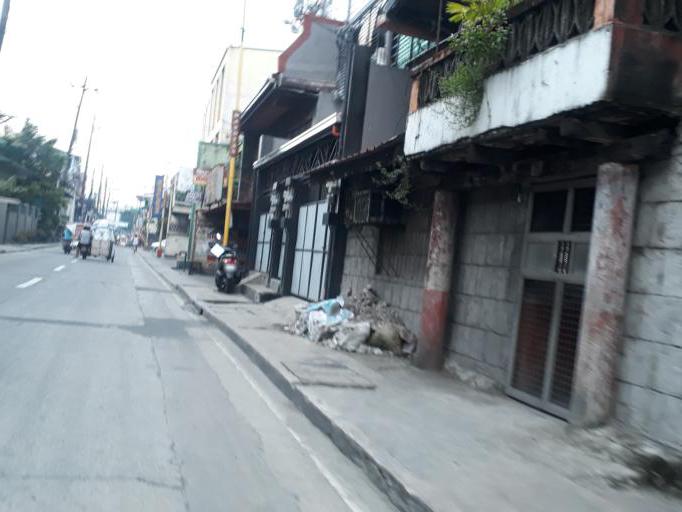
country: PH
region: Metro Manila
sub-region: Caloocan City
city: Niugan
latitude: 14.6538
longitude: 120.9492
